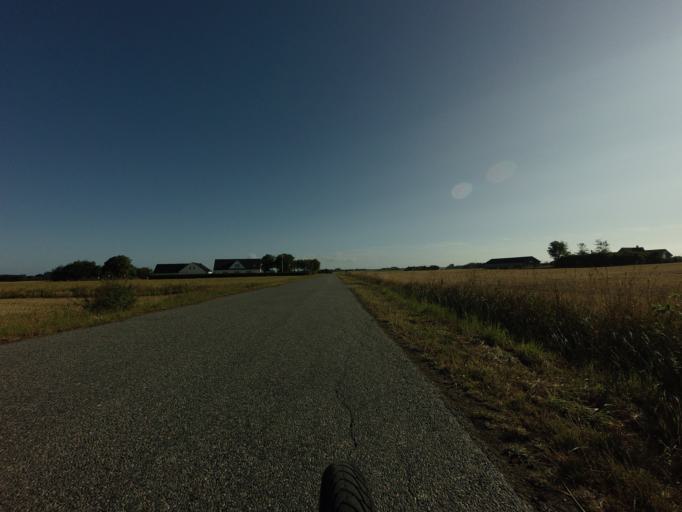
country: DK
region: North Denmark
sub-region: Hjorring Kommune
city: Vra
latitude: 57.3815
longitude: 9.9216
